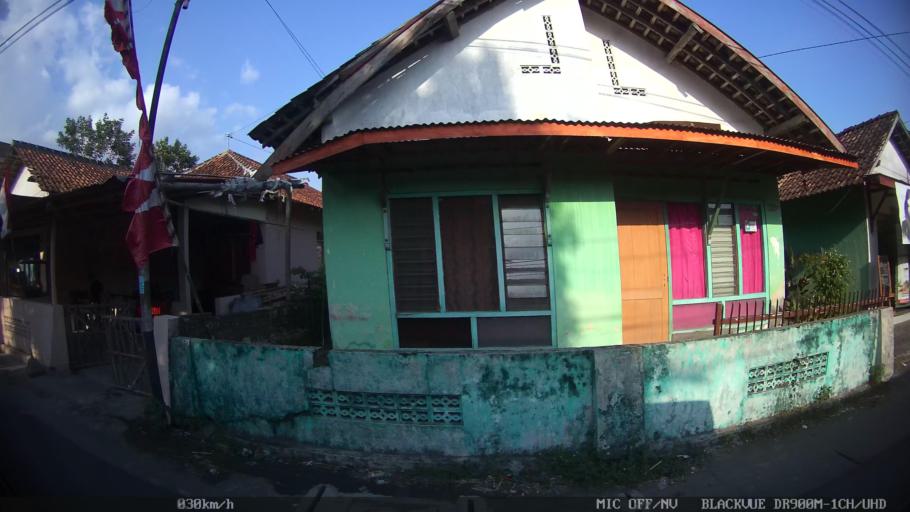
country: ID
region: Daerah Istimewa Yogyakarta
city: Gamping Lor
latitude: -7.7990
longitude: 110.3358
